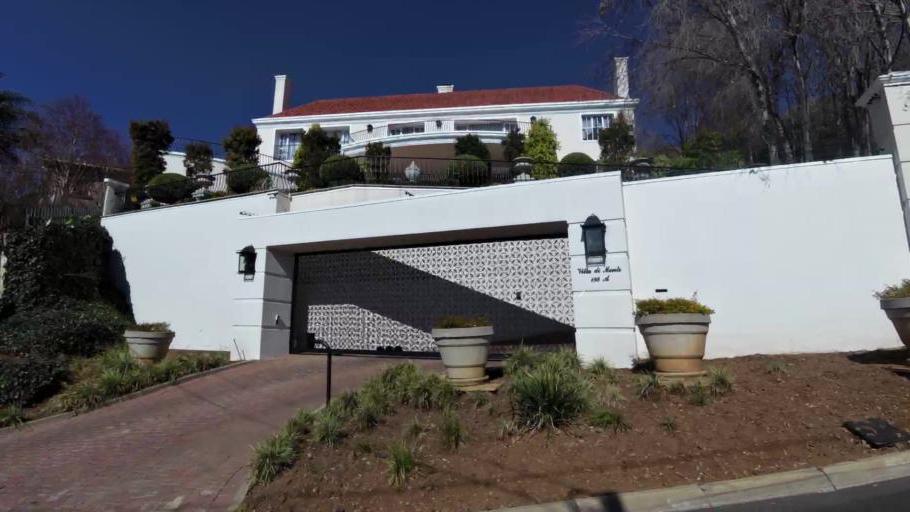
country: ZA
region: Gauteng
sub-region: City of Johannesburg Metropolitan Municipality
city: Johannesburg
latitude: -26.1422
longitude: 27.9702
